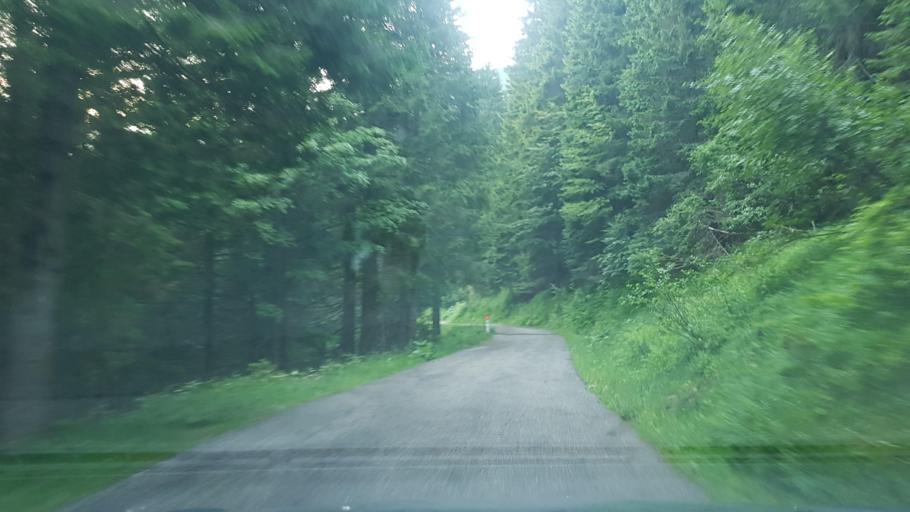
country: IT
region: Friuli Venezia Giulia
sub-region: Provincia di Udine
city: Paularo
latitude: 46.5752
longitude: 13.1563
